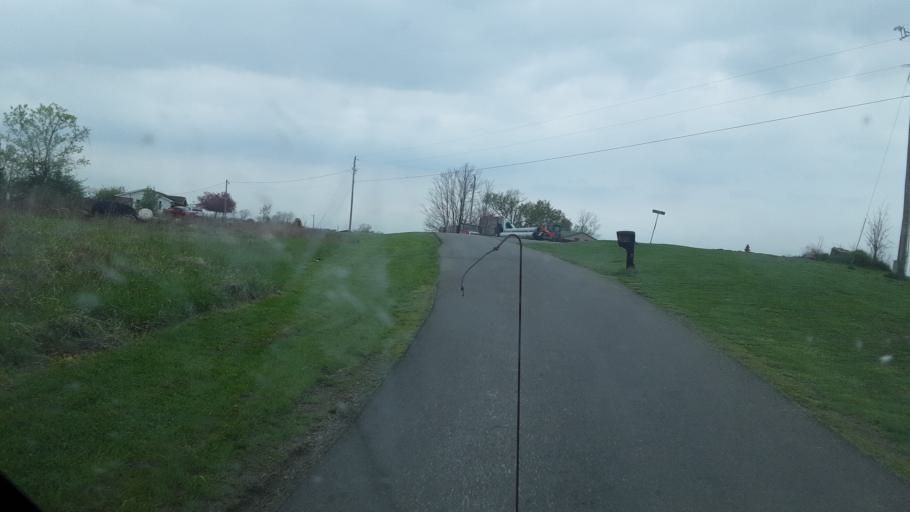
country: US
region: Kentucky
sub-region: Owen County
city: Owenton
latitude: 38.6726
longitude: -84.7839
